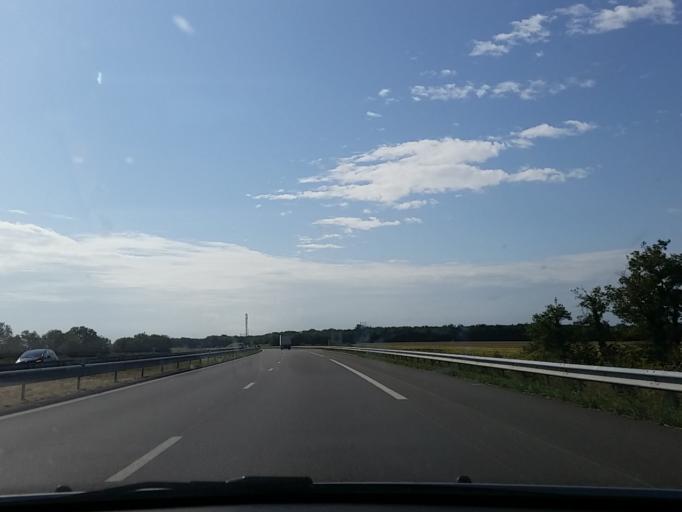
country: FR
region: Centre
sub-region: Departement du Cher
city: Plaimpied-Givaudins
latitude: 46.9904
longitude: 2.4092
